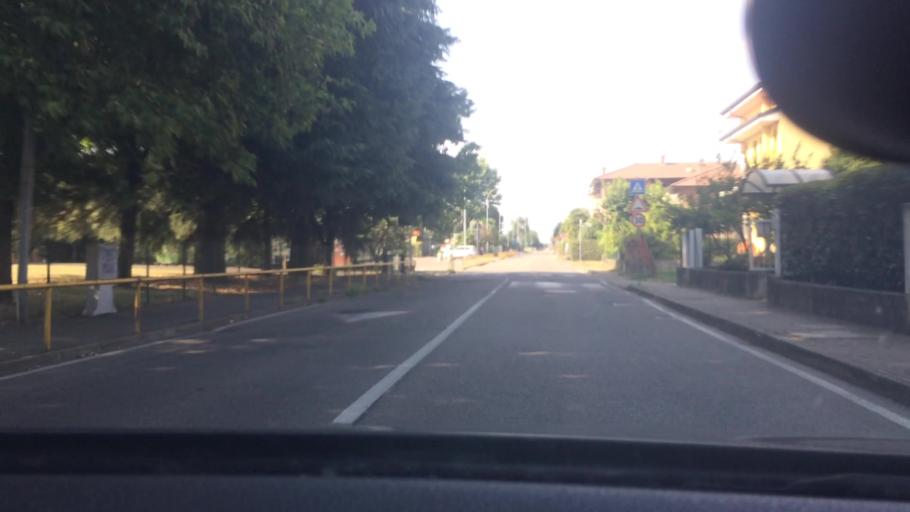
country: IT
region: Lombardy
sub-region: Provincia di Monza e Brianza
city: Ceriano Laghetto
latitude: 45.6318
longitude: 9.0756
